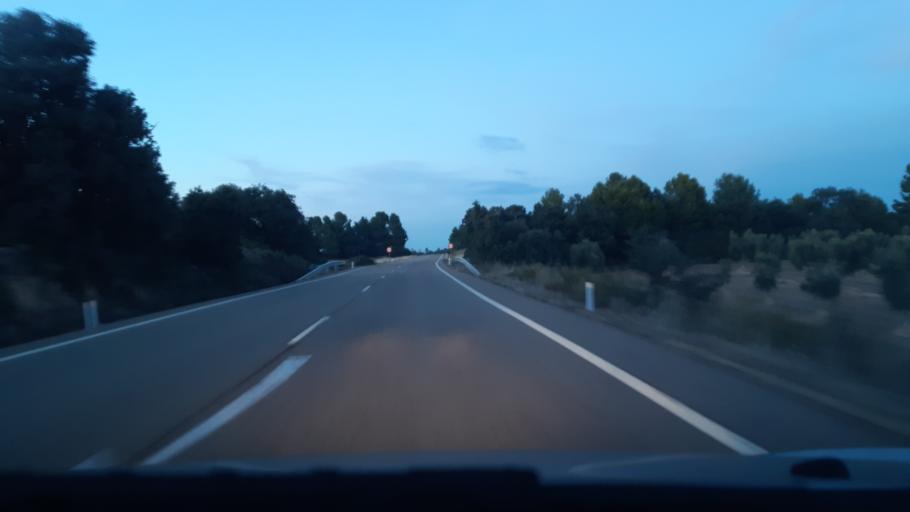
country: ES
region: Aragon
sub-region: Provincia de Teruel
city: Lledo
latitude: 40.9475
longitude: 0.2229
